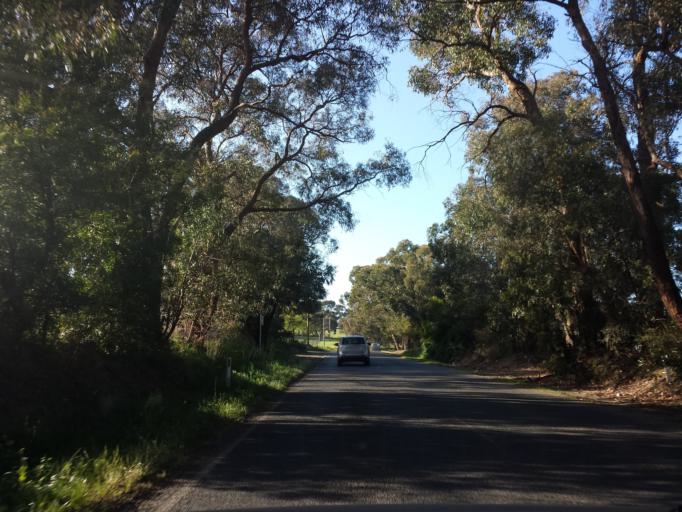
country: AU
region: Victoria
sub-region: Yarra Ranges
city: Belgrave South
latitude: -37.9634
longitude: 145.3624
